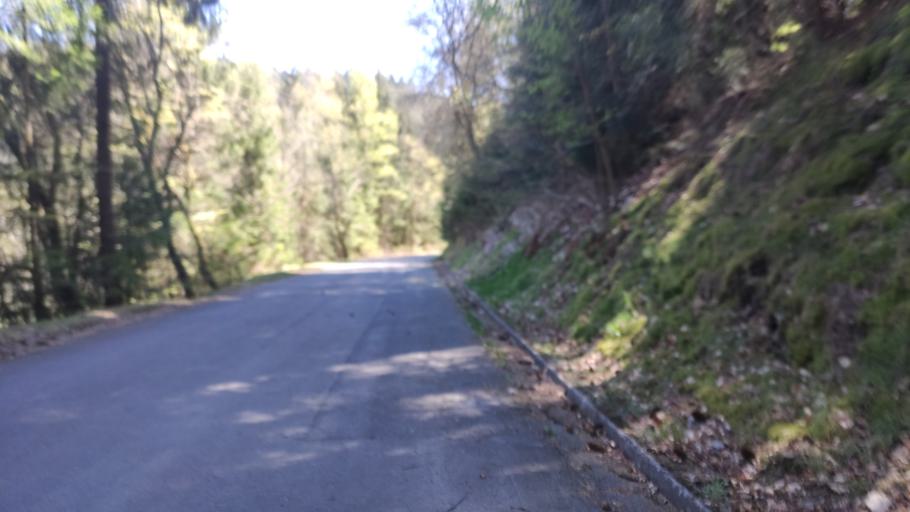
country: DE
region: Bavaria
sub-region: Upper Franconia
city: Nordhalben
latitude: 50.3572
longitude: 11.4857
